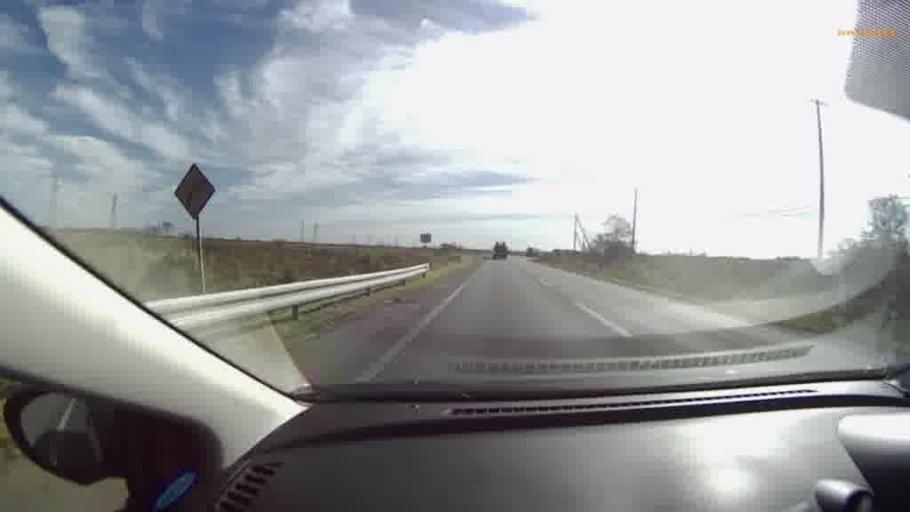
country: JP
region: Hokkaido
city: Kushiro
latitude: 43.0340
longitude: 144.2535
